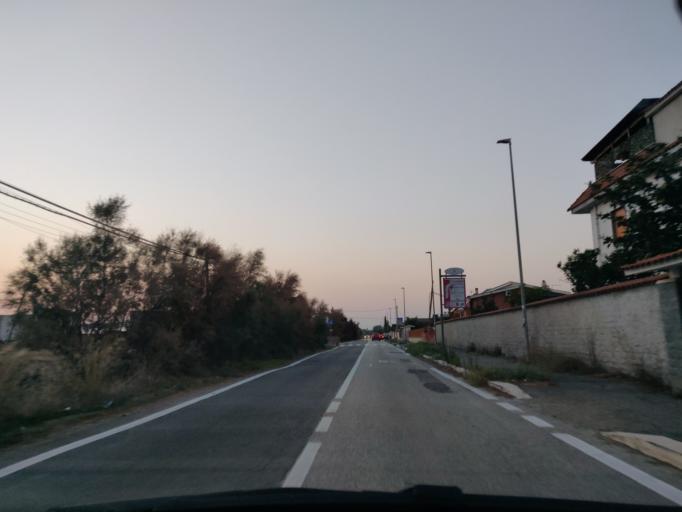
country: IT
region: Latium
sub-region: Citta metropolitana di Roma Capitale
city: Npp 23 (Parco Leonardo)
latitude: 41.8168
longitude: 12.2981
